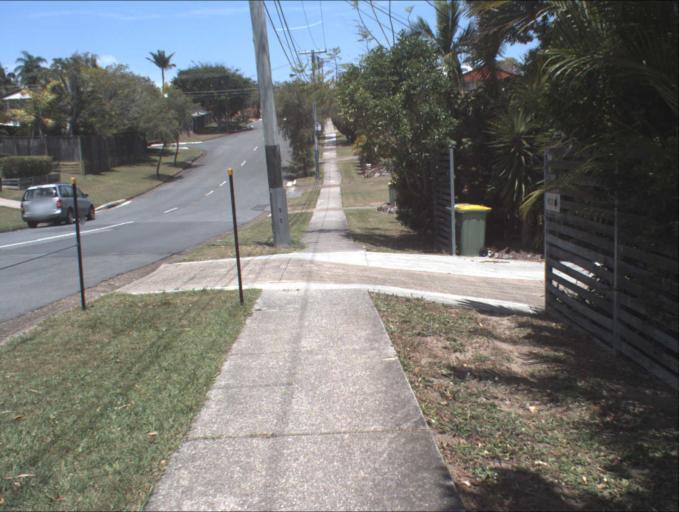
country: AU
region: Queensland
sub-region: Logan
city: Rochedale South
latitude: -27.5948
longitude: 153.1376
